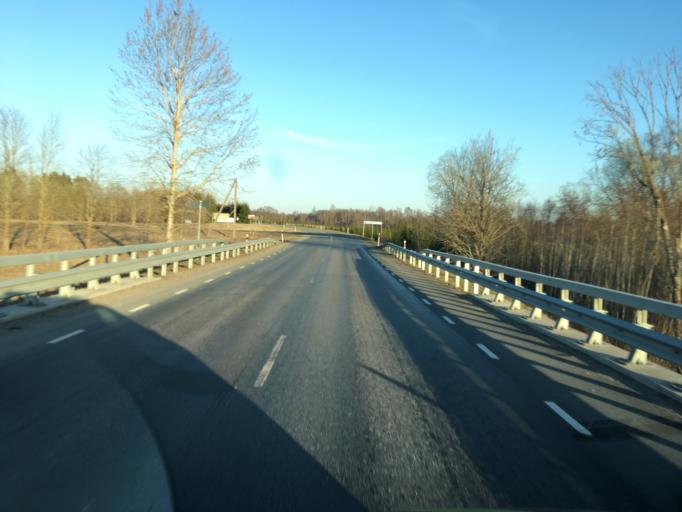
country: EE
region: Raplamaa
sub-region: Rapla vald
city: Rapla
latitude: 59.0811
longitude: 24.8284
